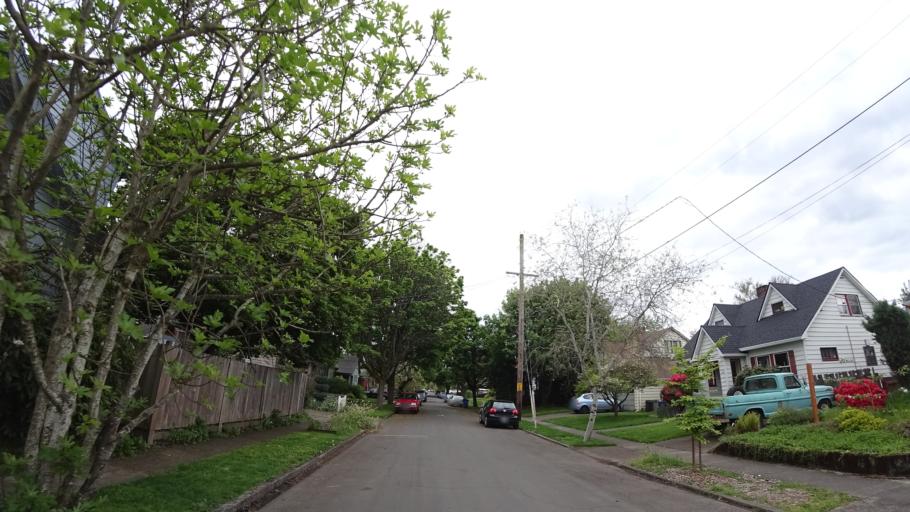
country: US
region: Oregon
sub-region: Clackamas County
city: Milwaukie
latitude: 45.4815
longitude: -122.6444
